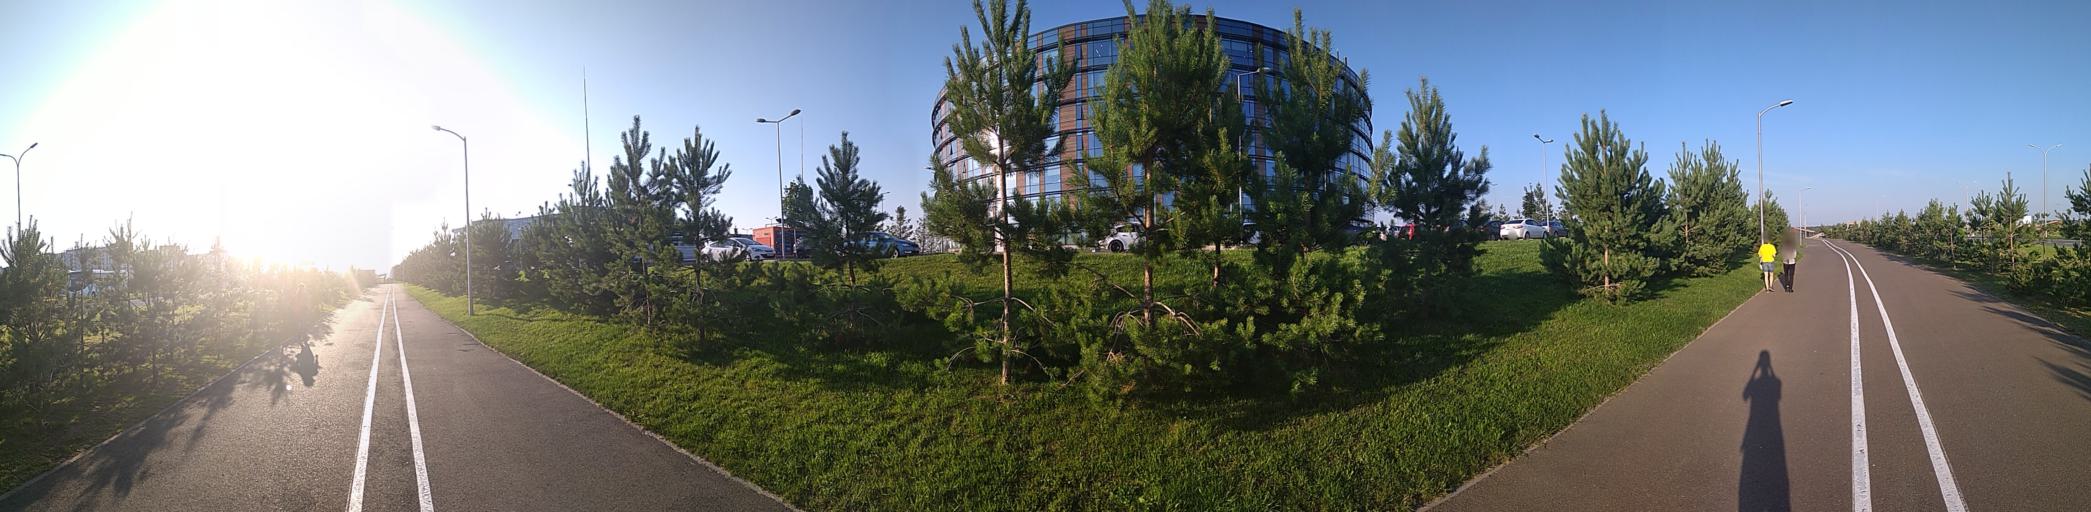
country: RU
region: Tatarstan
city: Sviyazhsk
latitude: 55.7501
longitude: 48.7481
